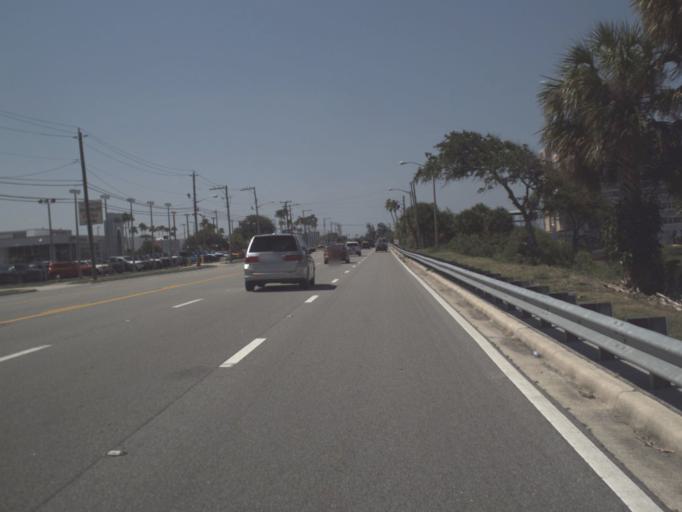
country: US
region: Florida
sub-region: Brevard County
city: Melbourne
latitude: 28.0953
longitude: -80.6107
